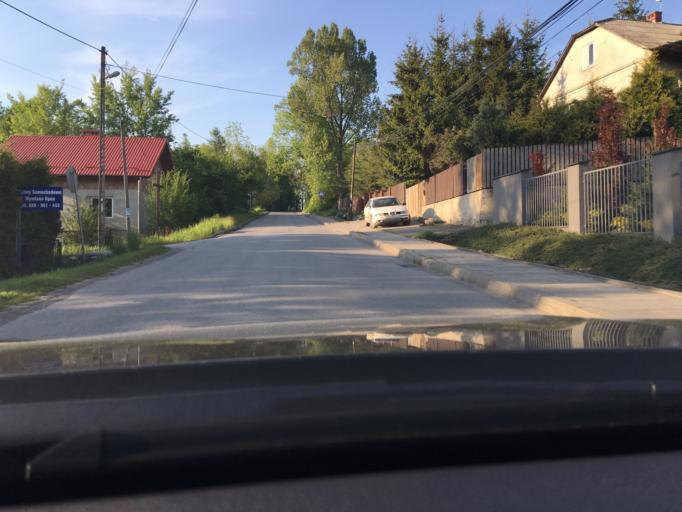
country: PL
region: Lesser Poland Voivodeship
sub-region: Powiat krakowski
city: Jerzmanowice
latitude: 50.2097
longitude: 19.7442
